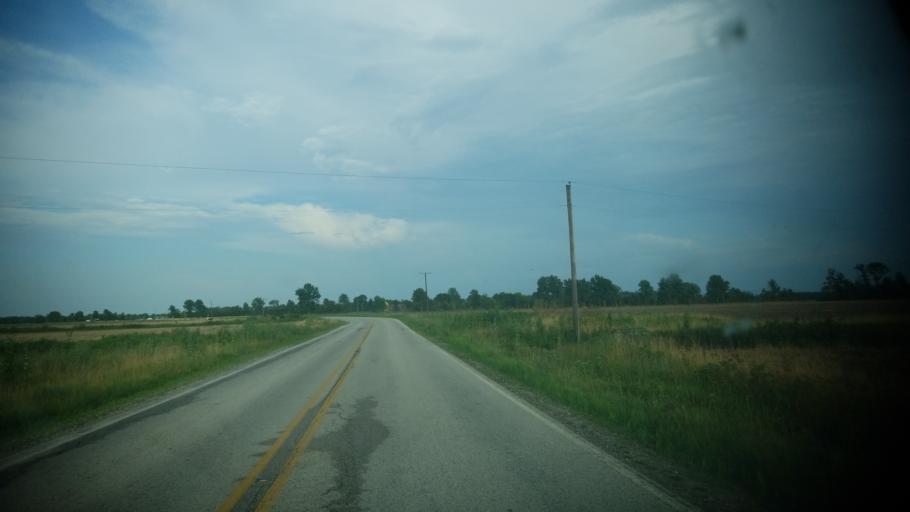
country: US
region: Illinois
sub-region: Clay County
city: Flora
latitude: 38.5169
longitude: -88.4712
